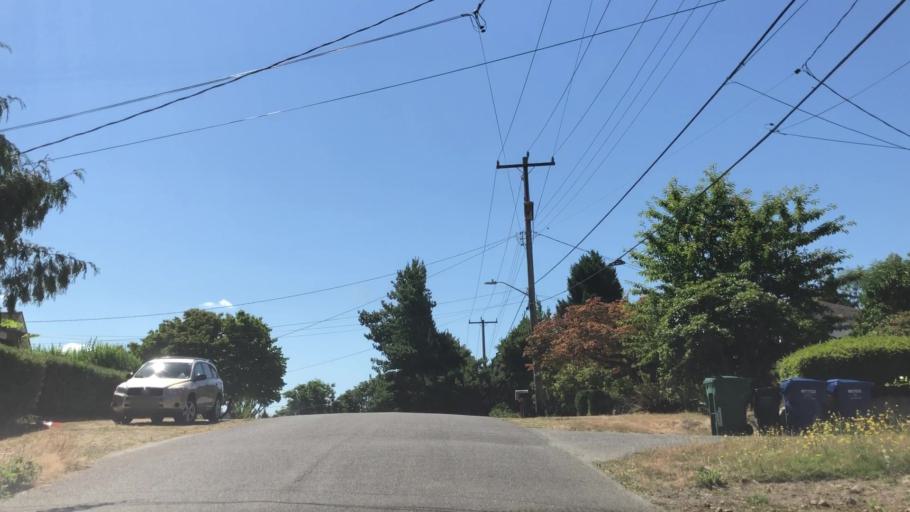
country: US
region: Washington
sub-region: King County
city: Shoreline
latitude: 47.7045
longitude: -122.3375
